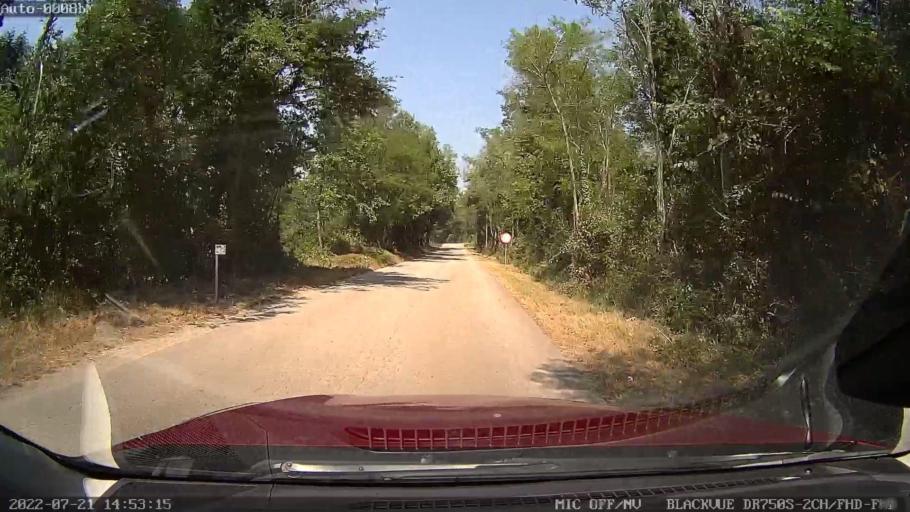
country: HR
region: Istarska
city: Pazin
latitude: 45.1805
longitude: 13.9308
